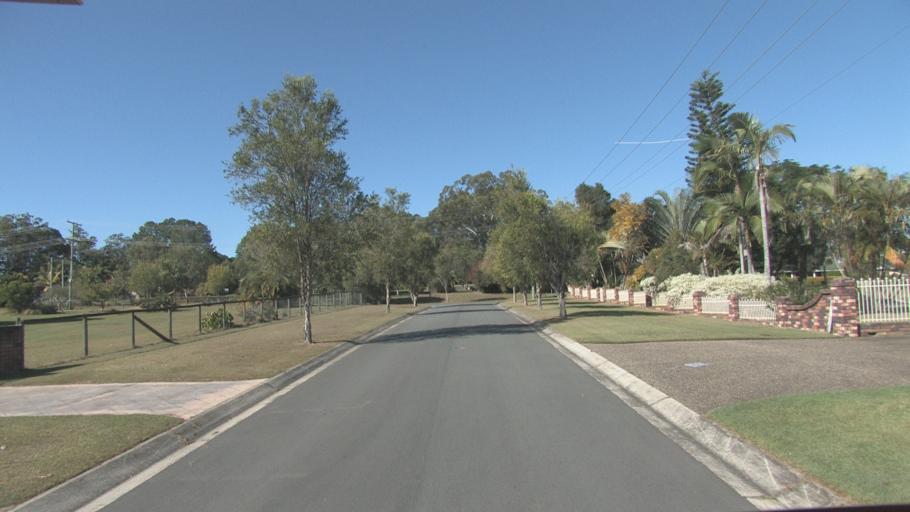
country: AU
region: Queensland
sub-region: Logan
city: Park Ridge South
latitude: -27.6966
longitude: 153.0317
